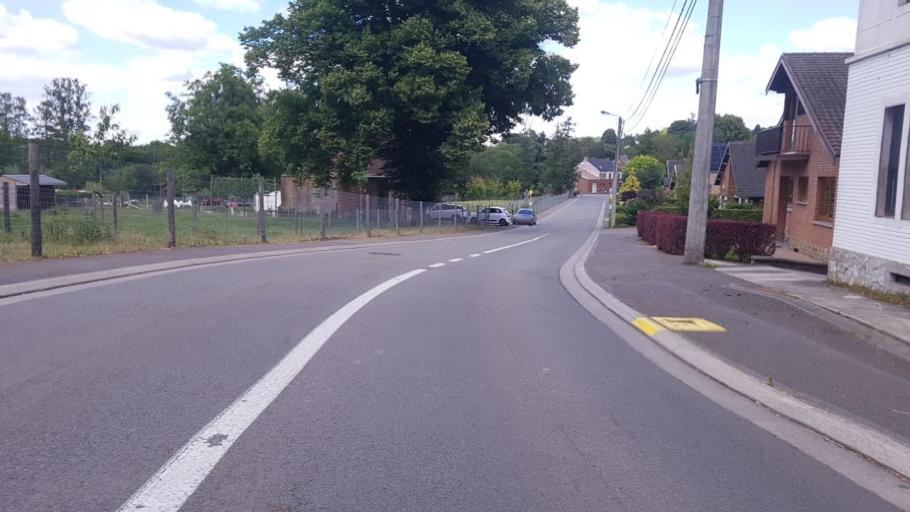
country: BE
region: Wallonia
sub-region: Province du Hainaut
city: Charleroi
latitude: 50.3505
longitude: 4.4078
